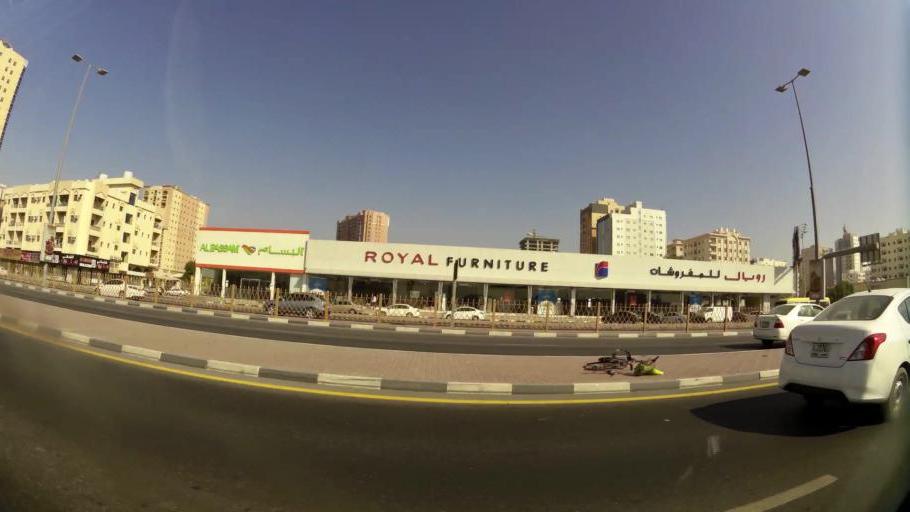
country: AE
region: Ajman
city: Ajman
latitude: 25.3844
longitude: 55.4659
